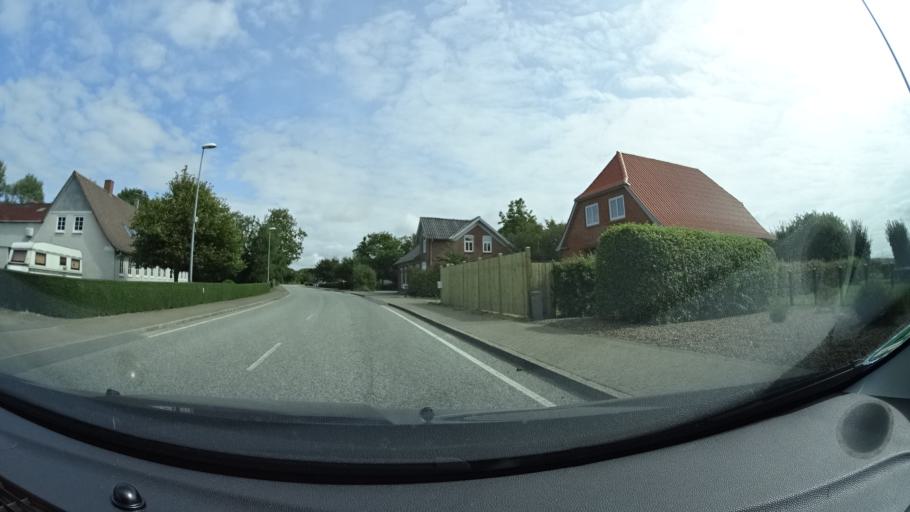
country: DK
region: South Denmark
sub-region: Tonder Kommune
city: Sherrebek
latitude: 55.0760
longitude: 8.6658
